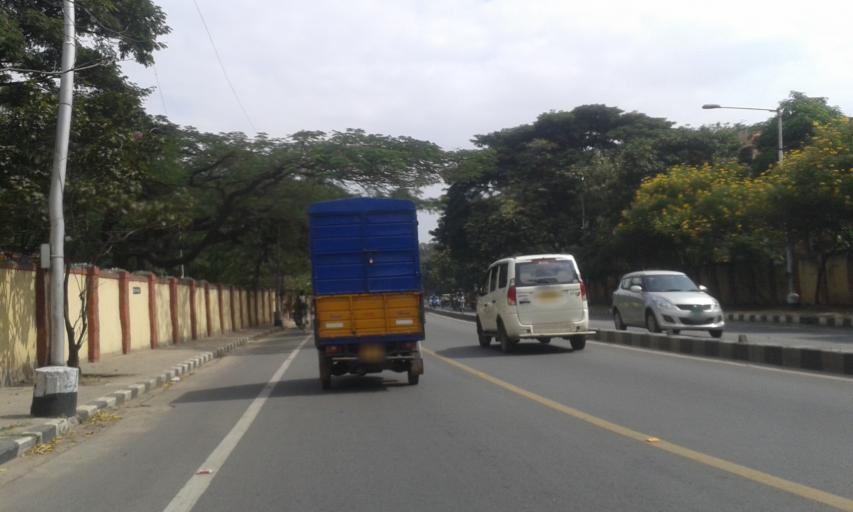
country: IN
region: Karnataka
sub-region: Bangalore Urban
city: Bangalore
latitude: 12.9672
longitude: 77.6230
